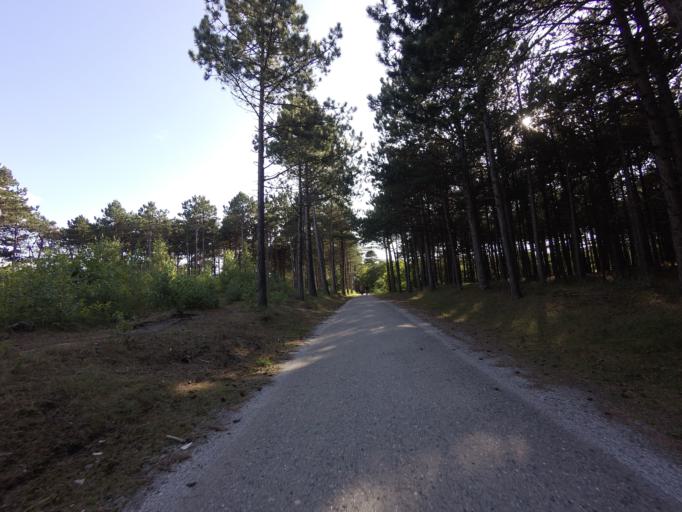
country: NL
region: Friesland
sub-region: Gemeente Terschelling
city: West-Terschelling
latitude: 53.3820
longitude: 5.2241
